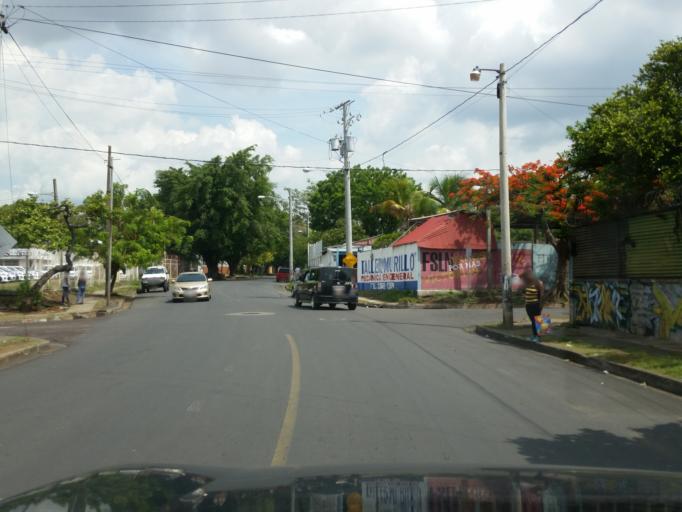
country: NI
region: Managua
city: Ciudad Sandino
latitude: 12.1433
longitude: -86.2995
